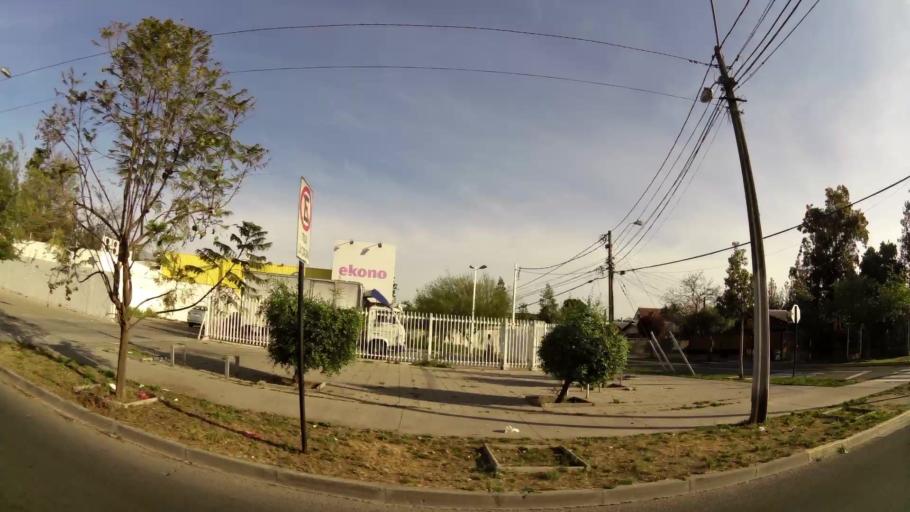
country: CL
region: Santiago Metropolitan
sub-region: Provincia de Cordillera
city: Puente Alto
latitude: -33.5530
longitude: -70.5747
